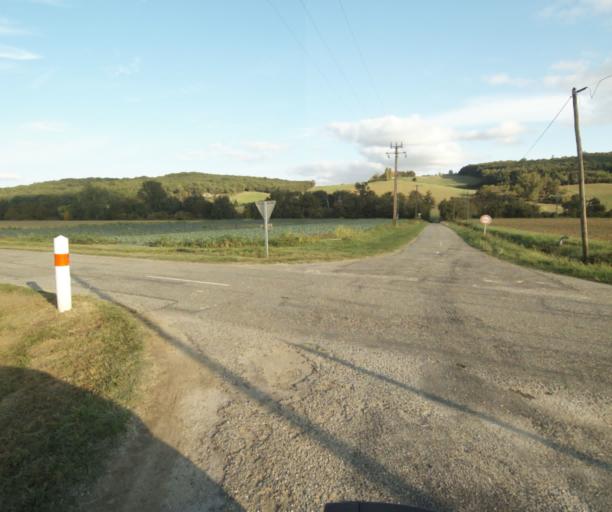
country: FR
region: Midi-Pyrenees
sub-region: Departement de la Haute-Garonne
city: Launac
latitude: 43.8099
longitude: 1.1148
